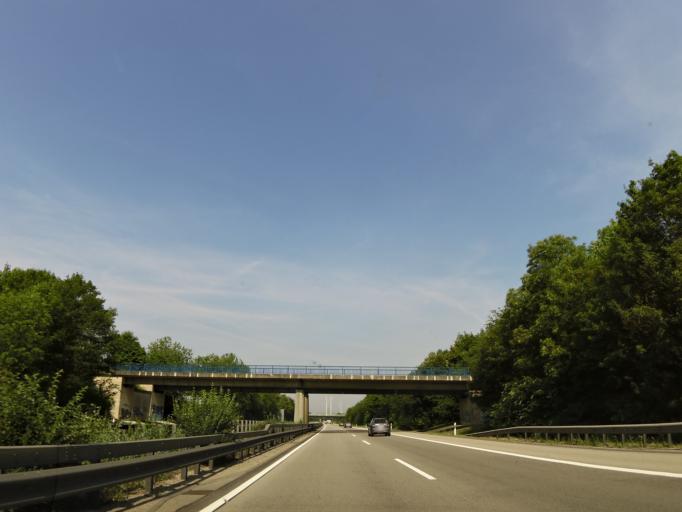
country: DE
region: Rheinland-Pfalz
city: Lonsheim
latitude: 49.7932
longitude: 8.0817
